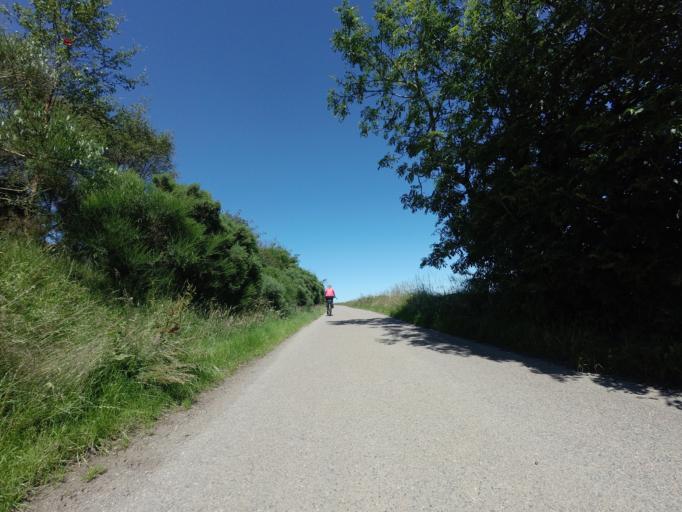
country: GB
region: Scotland
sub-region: Aberdeenshire
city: Macduff
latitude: 57.6462
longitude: -2.5049
